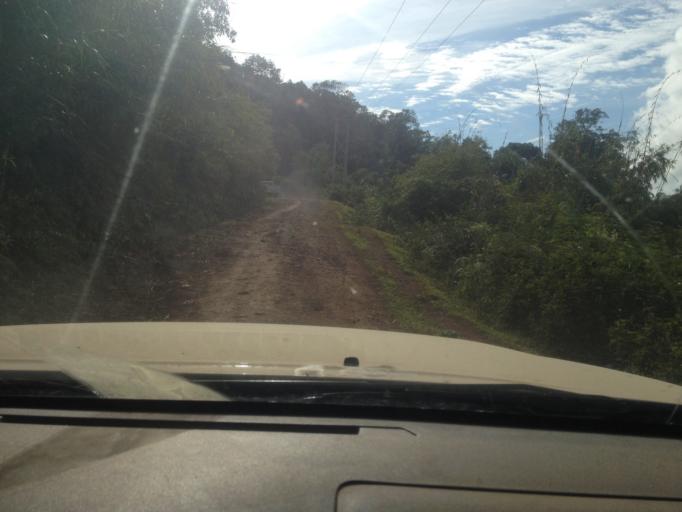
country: TH
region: Nan
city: Chaloem Phra Kiat
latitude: 19.9629
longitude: 101.0217
